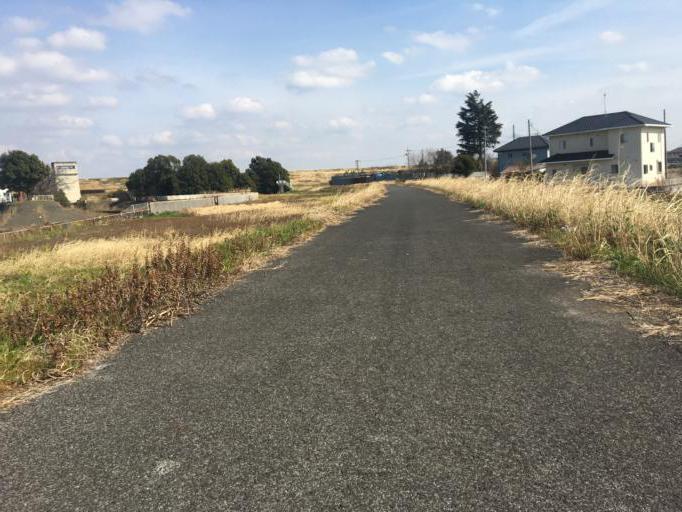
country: JP
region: Saitama
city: Shiki
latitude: 35.8709
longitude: 139.5693
